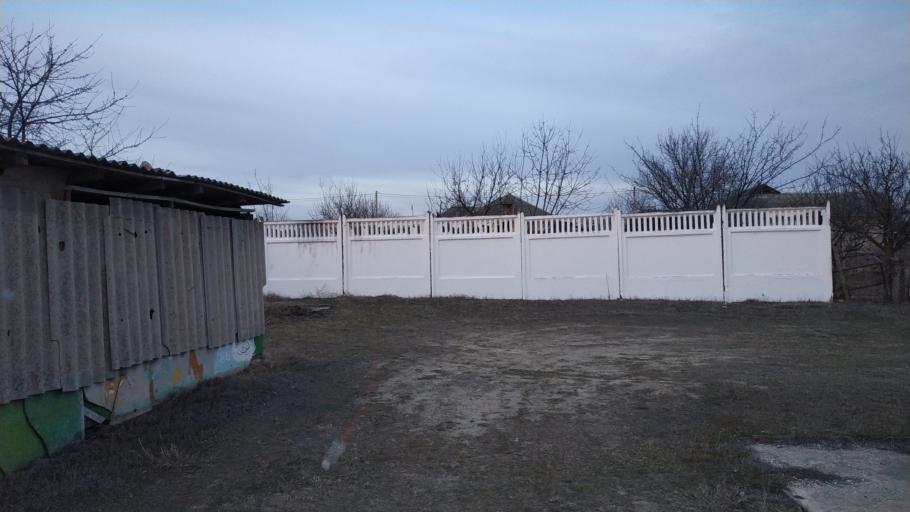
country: MD
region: Hincesti
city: Dancu
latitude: 46.7402
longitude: 28.2226
